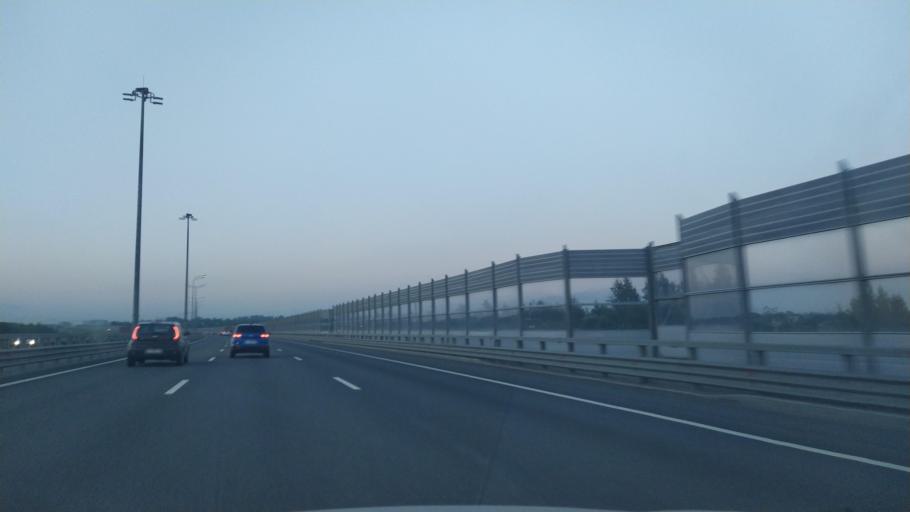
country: RU
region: St.-Petersburg
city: Levashovo
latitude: 60.0847
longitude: 30.2228
